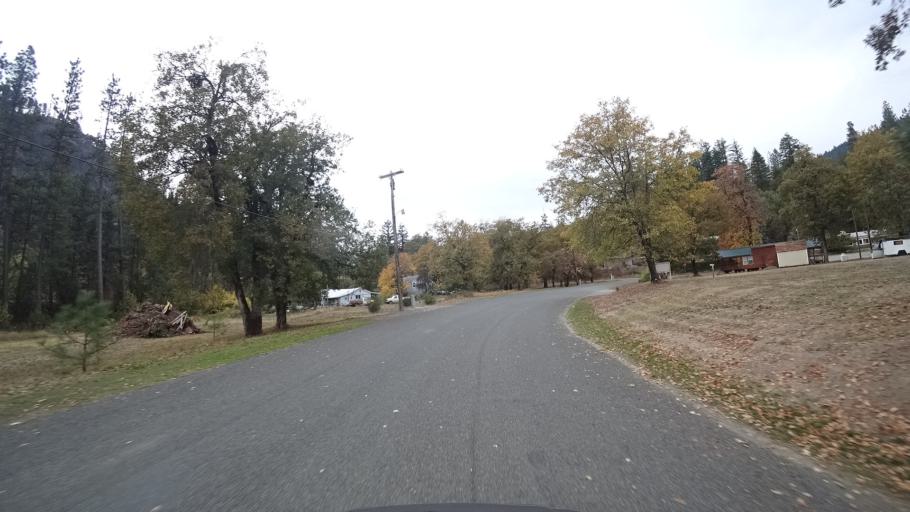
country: US
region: California
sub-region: Siskiyou County
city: Happy Camp
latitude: 41.7902
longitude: -123.3819
